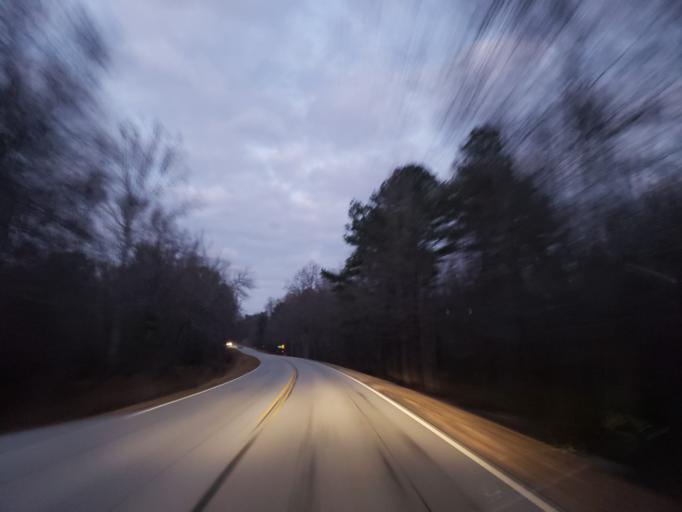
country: US
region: Georgia
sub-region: Carroll County
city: Temple
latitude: 33.8122
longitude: -85.0474
